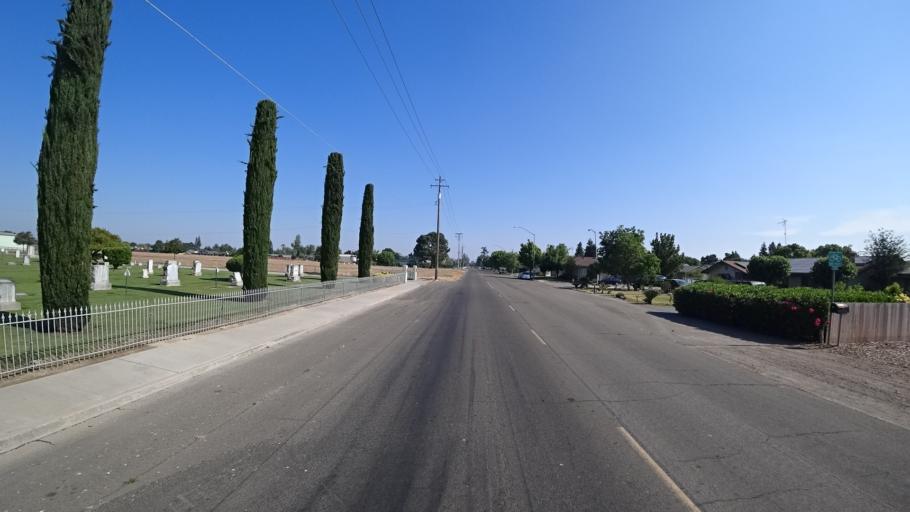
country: US
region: California
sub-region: Fresno County
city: Kingsburg
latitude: 36.5048
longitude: -119.5569
